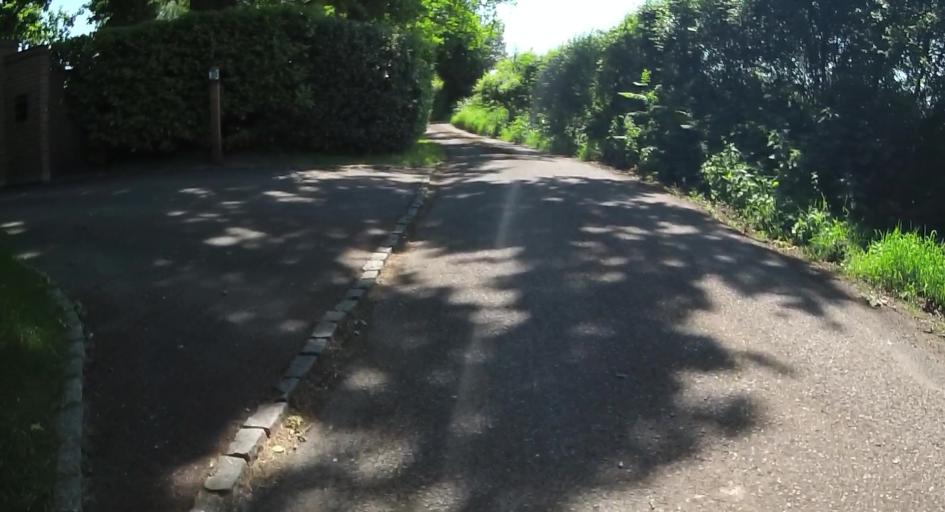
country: GB
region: England
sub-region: Hampshire
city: Kingsclere
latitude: 51.3487
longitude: -1.2746
